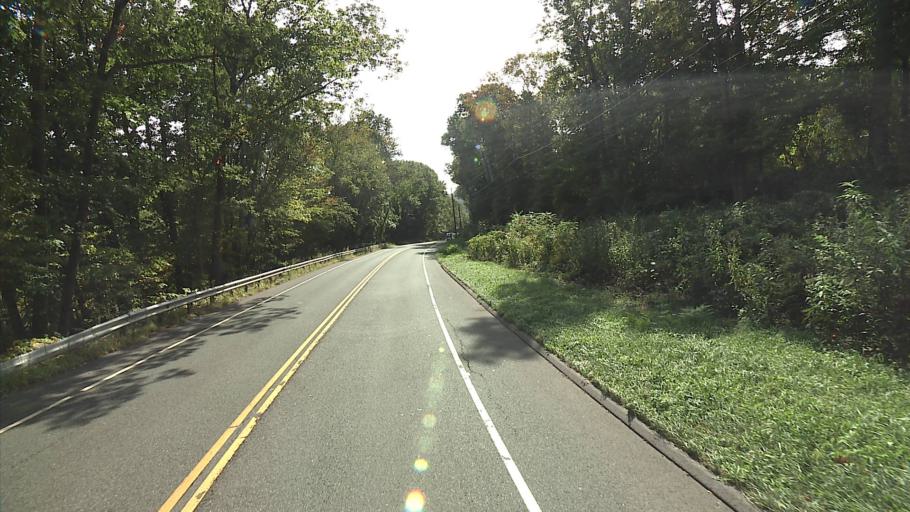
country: US
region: Connecticut
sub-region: New Haven County
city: Oxford
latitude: 41.3860
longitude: -73.1815
